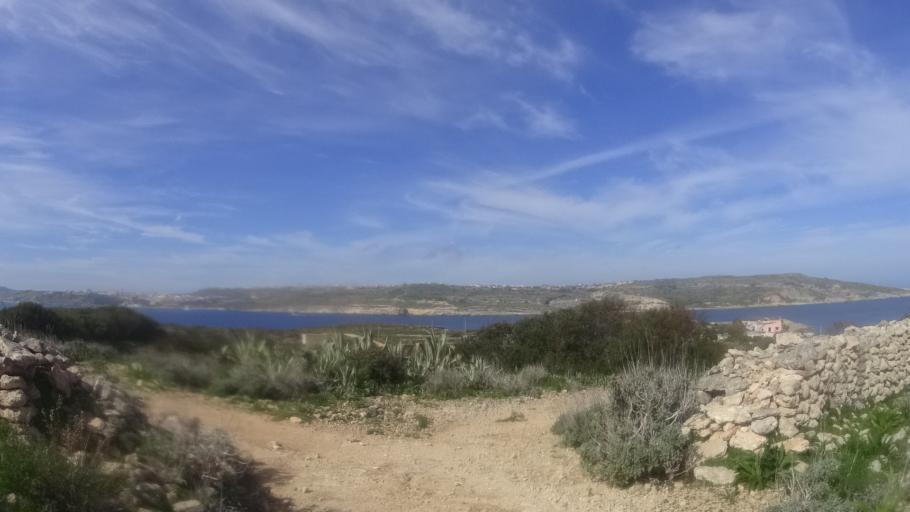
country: MT
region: Il-Qala
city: Qala
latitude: 36.0137
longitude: 14.3284
